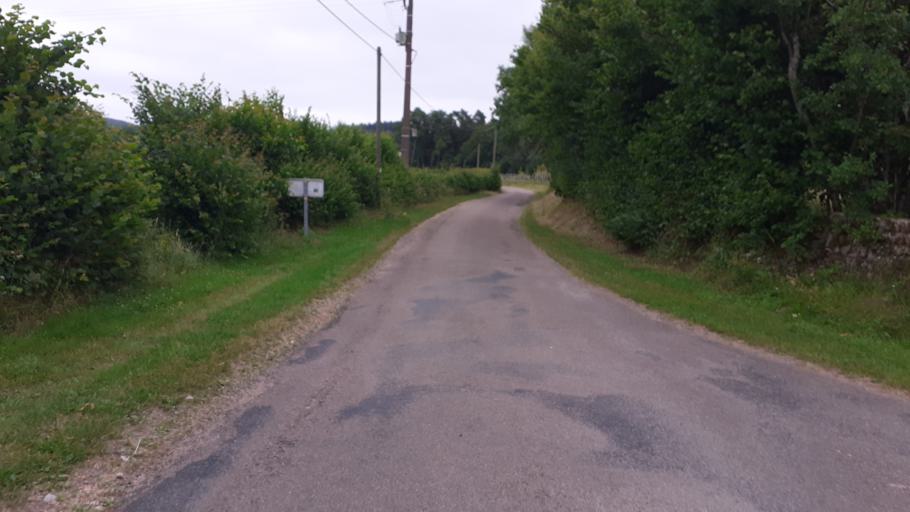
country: FR
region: Bourgogne
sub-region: Departement de la Cote-d'Or
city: Saulieu
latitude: 47.2726
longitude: 4.1403
